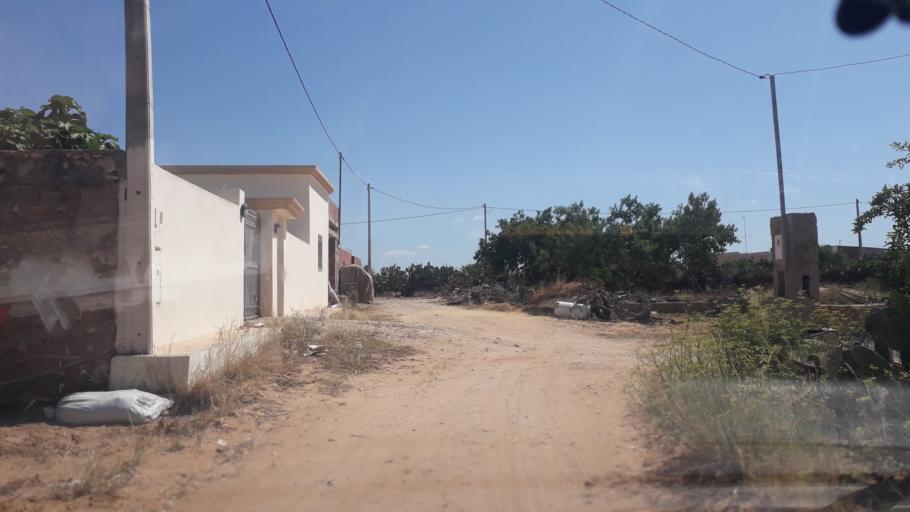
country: TN
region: Safaqis
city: Al Qarmadah
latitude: 34.8298
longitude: 10.7685
